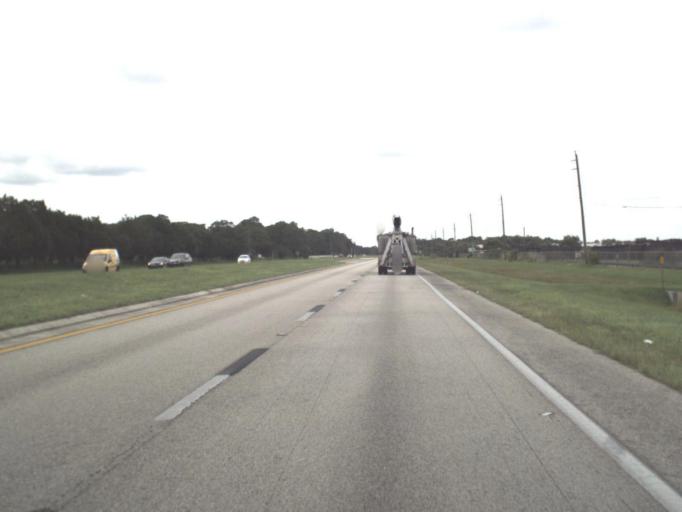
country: US
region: Florida
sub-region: Lee County
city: Alva
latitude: 26.7094
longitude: -81.6282
